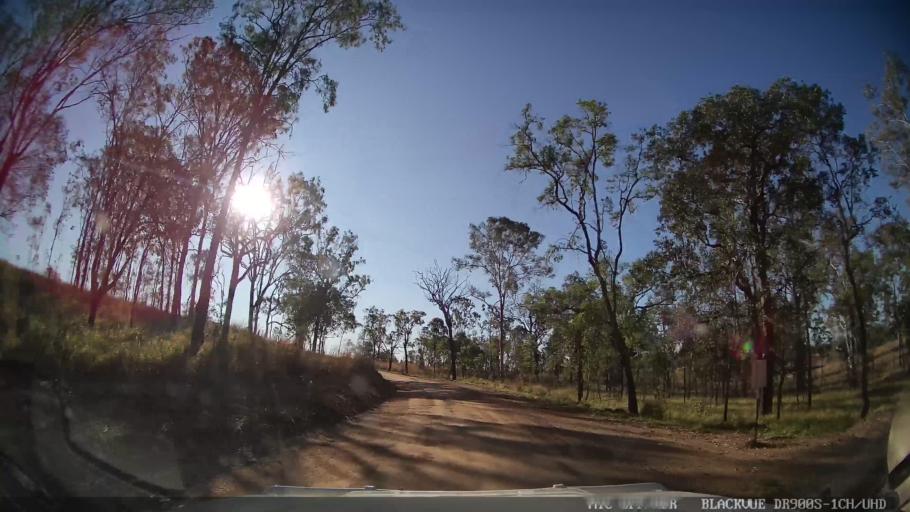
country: AU
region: Queensland
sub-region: Bundaberg
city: Sharon
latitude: -24.7880
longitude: 151.6070
